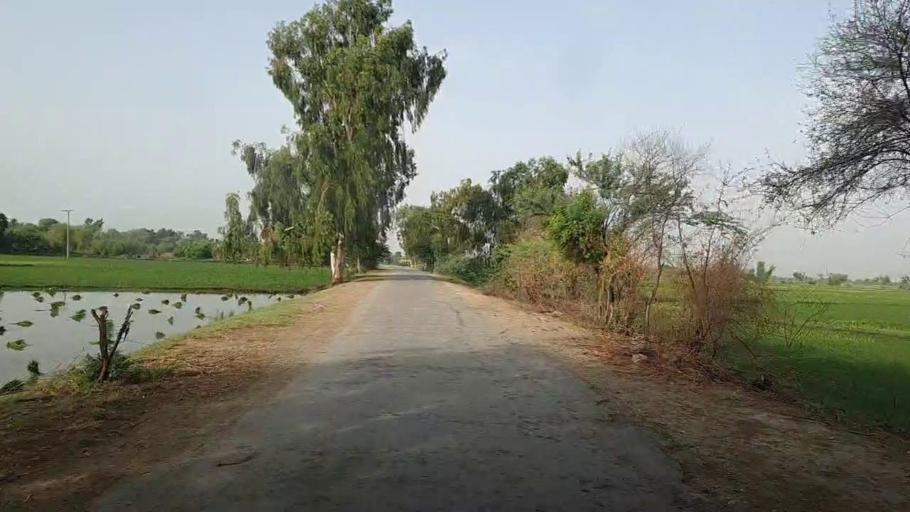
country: PK
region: Sindh
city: Khairpur Nathan Shah
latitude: 27.1206
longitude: 67.7892
